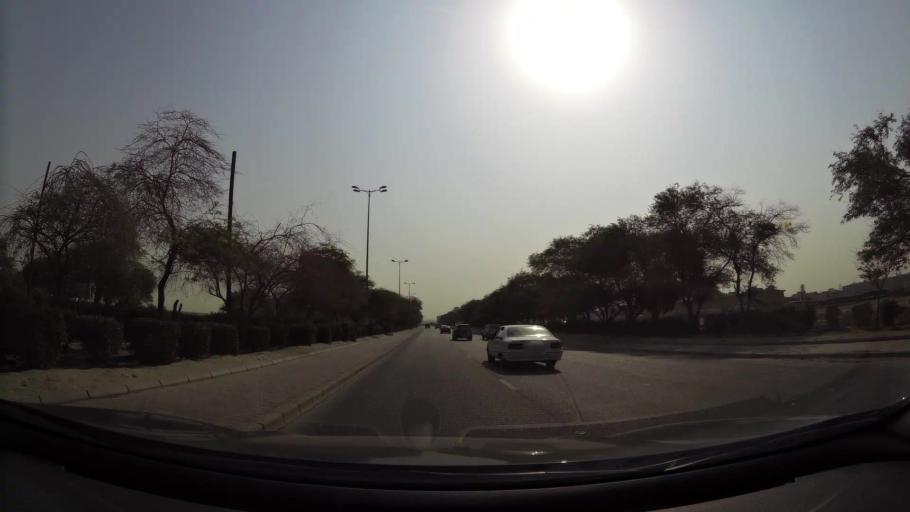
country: KW
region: Al Asimah
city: Ar Rabiyah
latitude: 29.2775
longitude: 47.8438
